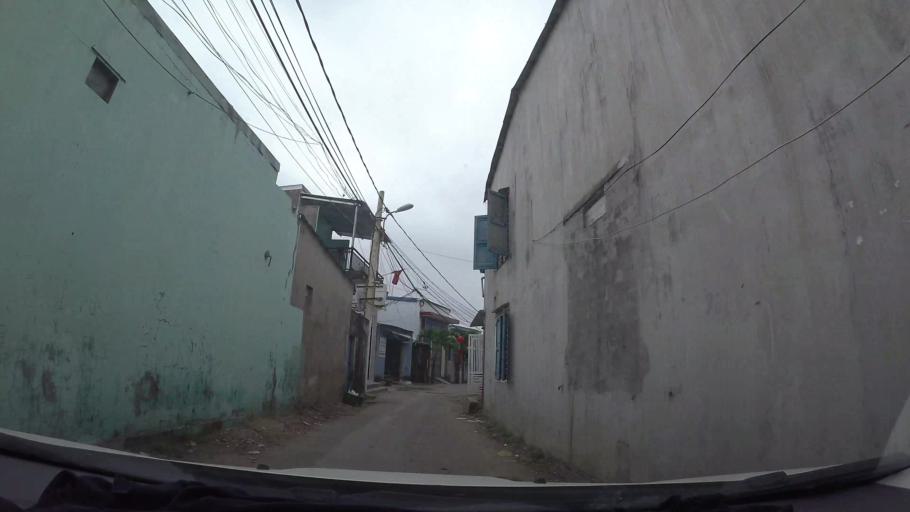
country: VN
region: Da Nang
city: Lien Chieu
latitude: 16.1216
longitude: 108.1176
